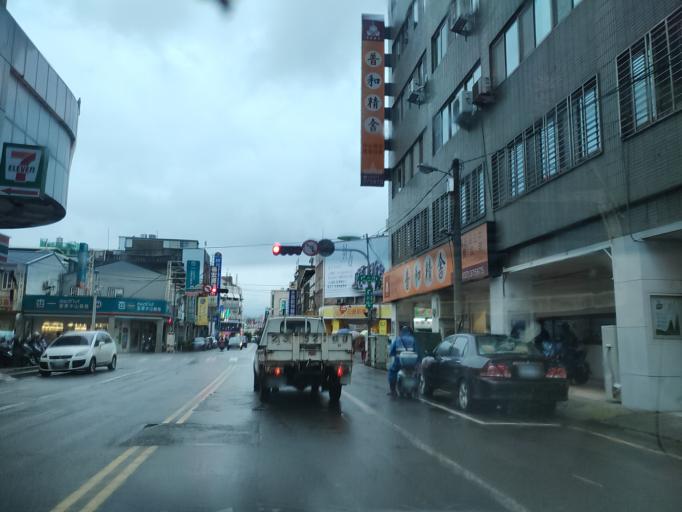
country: TW
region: Taiwan
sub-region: Miaoli
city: Miaoli
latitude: 24.5575
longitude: 120.8191
